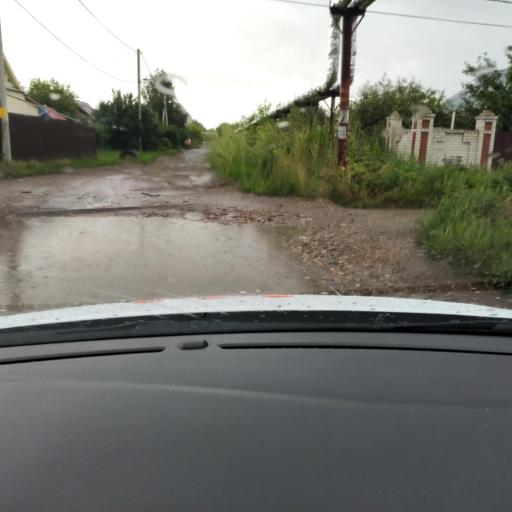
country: RU
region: Tatarstan
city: Vysokaya Gora
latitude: 55.8731
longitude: 49.2335
